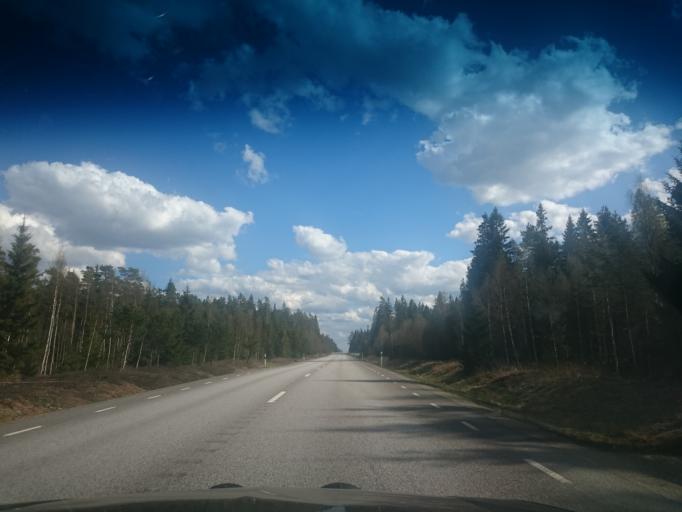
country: SE
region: Joenkoeping
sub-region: Vetlanda Kommun
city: Vetlanda
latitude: 57.2523
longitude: 15.1334
